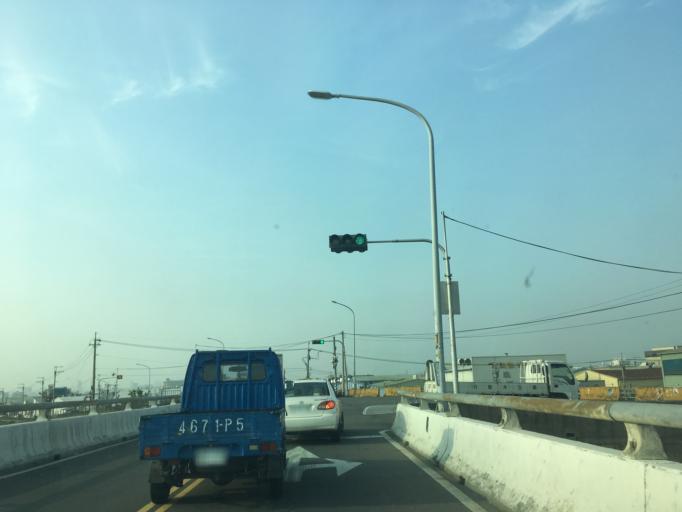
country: TW
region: Taiwan
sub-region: Taichung City
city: Taichung
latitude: 24.0739
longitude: 120.6800
